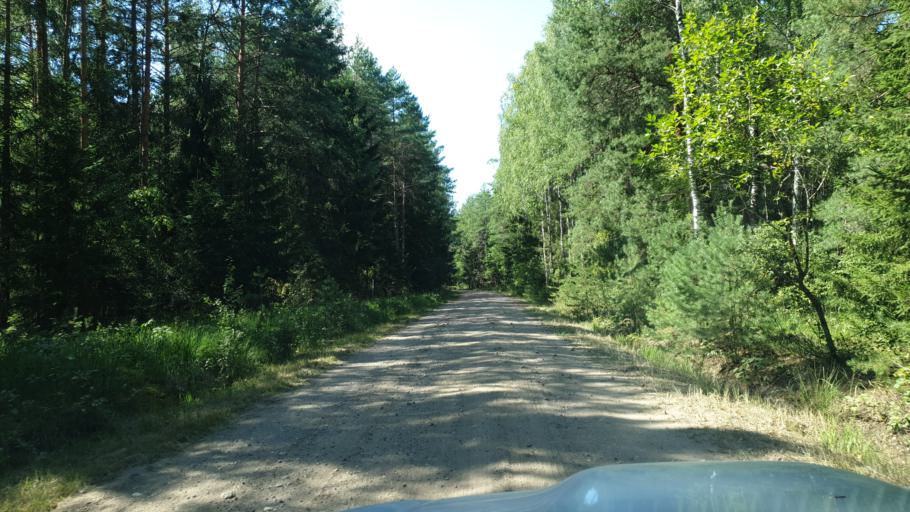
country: LT
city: Sirvintos
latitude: 54.9071
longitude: 24.9482
